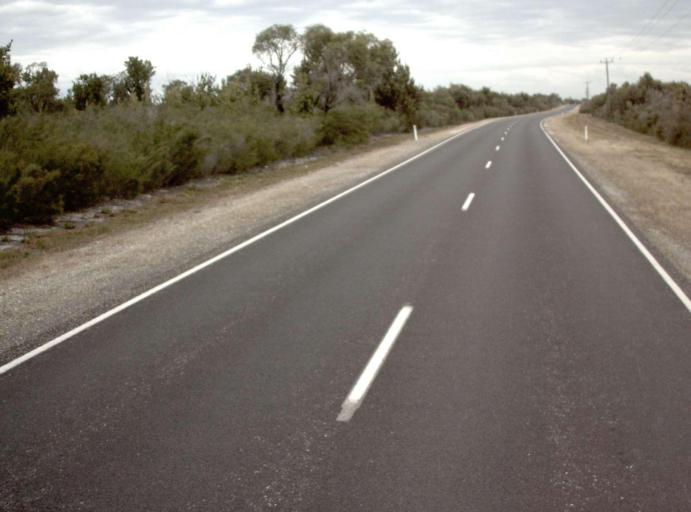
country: AU
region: Victoria
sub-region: Wellington
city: Sale
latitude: -38.1930
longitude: 147.3651
